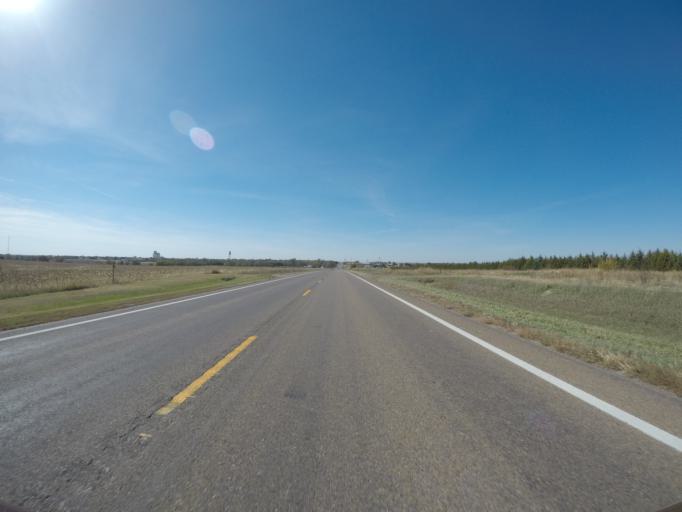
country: US
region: Kansas
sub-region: Smith County
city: Smith Center
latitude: 39.7710
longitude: -99.0198
